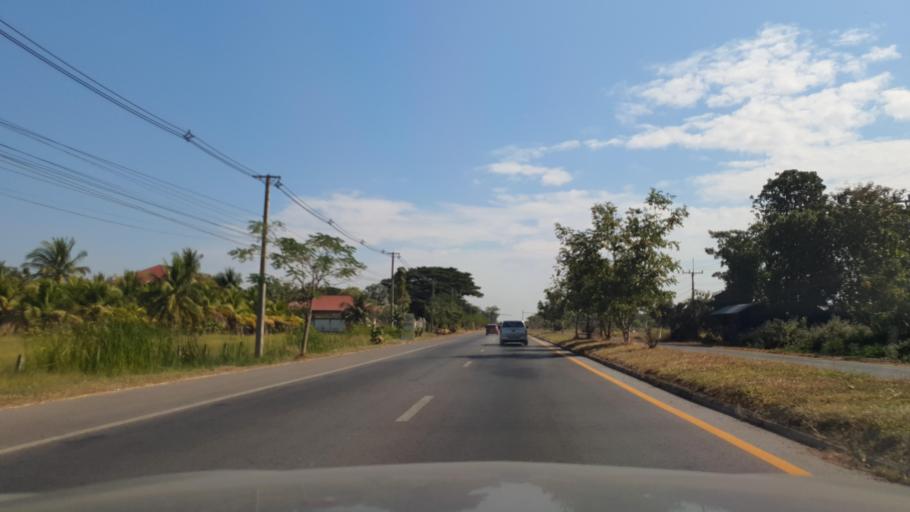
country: TH
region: Maha Sarakham
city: Chiang Yuen
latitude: 16.3796
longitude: 103.1934
